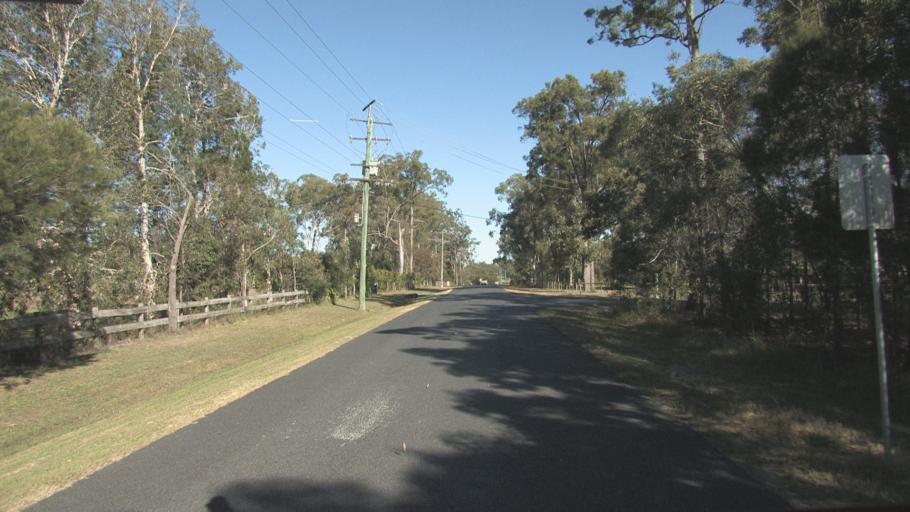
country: AU
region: Queensland
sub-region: Logan
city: Chambers Flat
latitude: -27.7305
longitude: 153.0723
